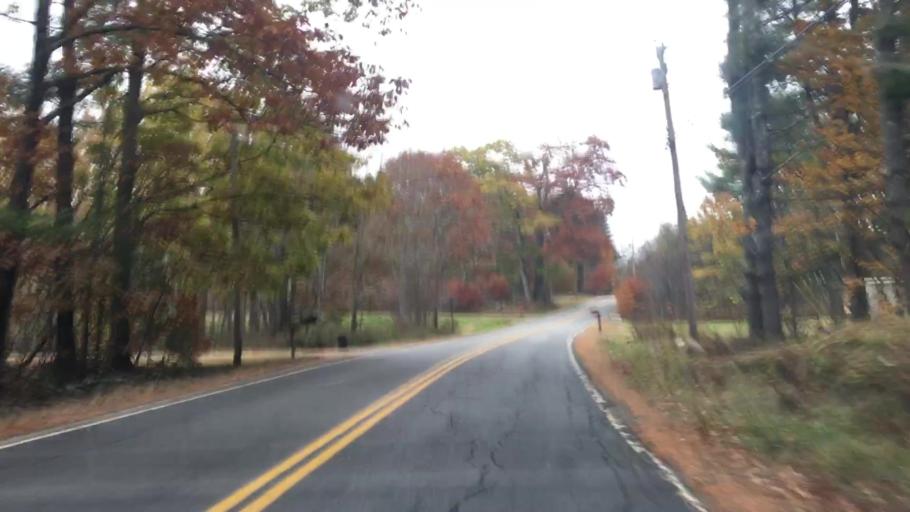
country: US
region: Maine
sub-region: Lincoln County
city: Whitefield
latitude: 44.1706
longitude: -69.6652
